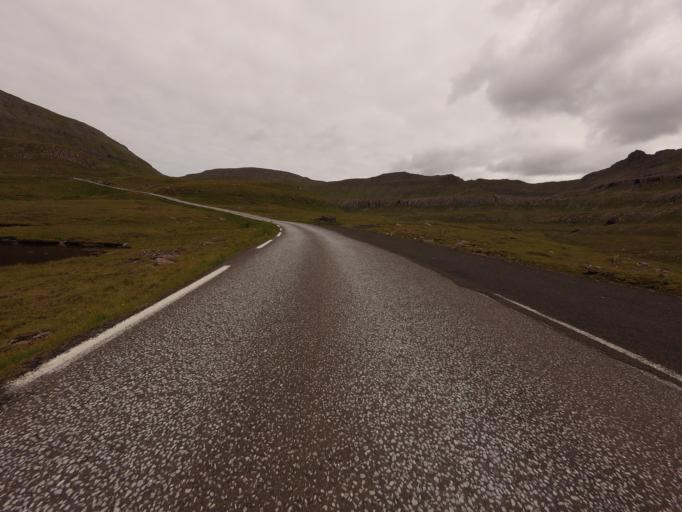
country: FO
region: Suduroy
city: Tvoroyri
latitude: 61.5166
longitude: -6.8696
